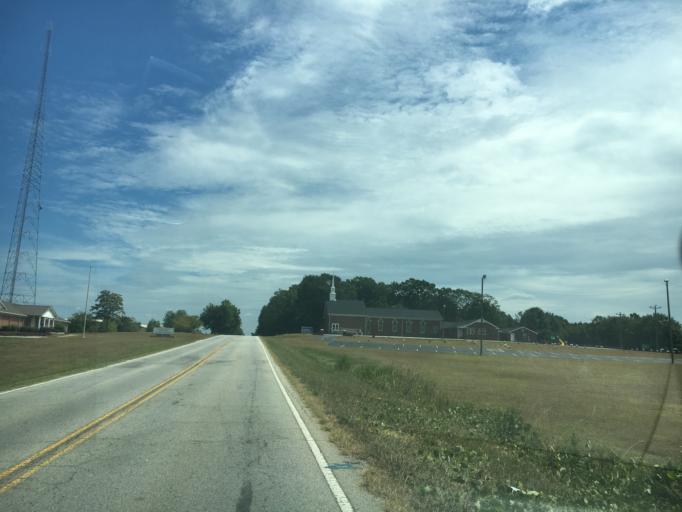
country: US
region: South Carolina
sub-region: Laurens County
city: Laurens
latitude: 34.5316
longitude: -82.0536
